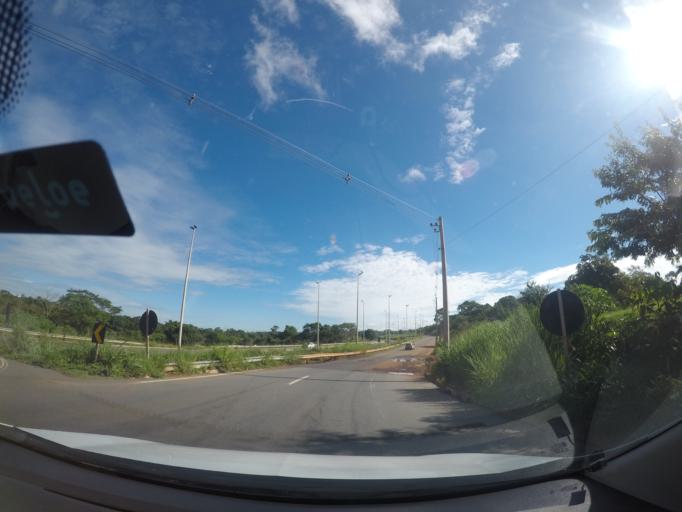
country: BR
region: Goias
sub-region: Goiania
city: Goiania
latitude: -16.6815
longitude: -49.1962
